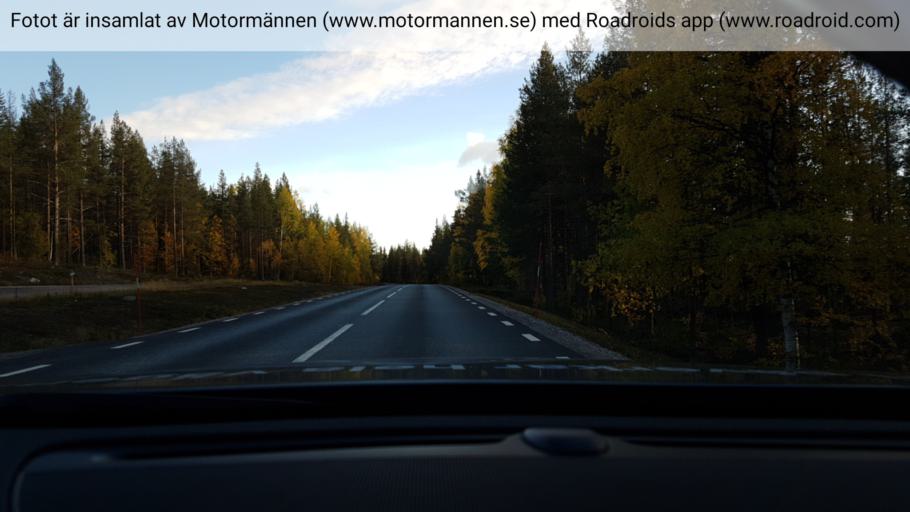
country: SE
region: Norrbotten
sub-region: Jokkmokks Kommun
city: Jokkmokk
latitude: 66.9458
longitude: 19.7984
